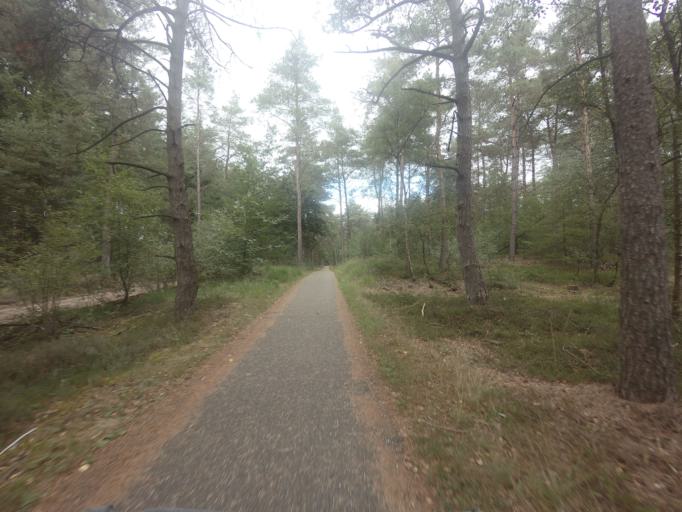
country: NL
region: Friesland
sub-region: Gemeente Weststellingwerf
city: Noordwolde
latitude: 52.9012
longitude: 6.2415
